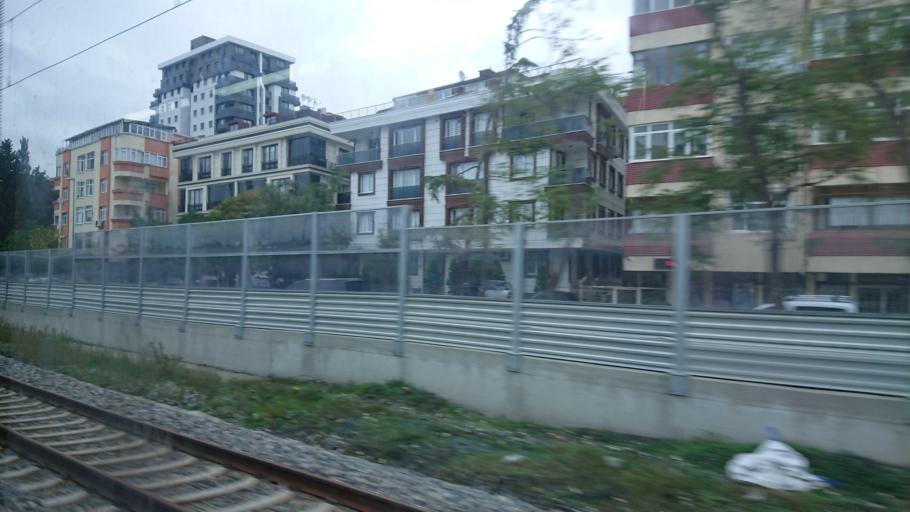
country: TR
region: Istanbul
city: Mahmutbey
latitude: 41.0000
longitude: 28.7680
